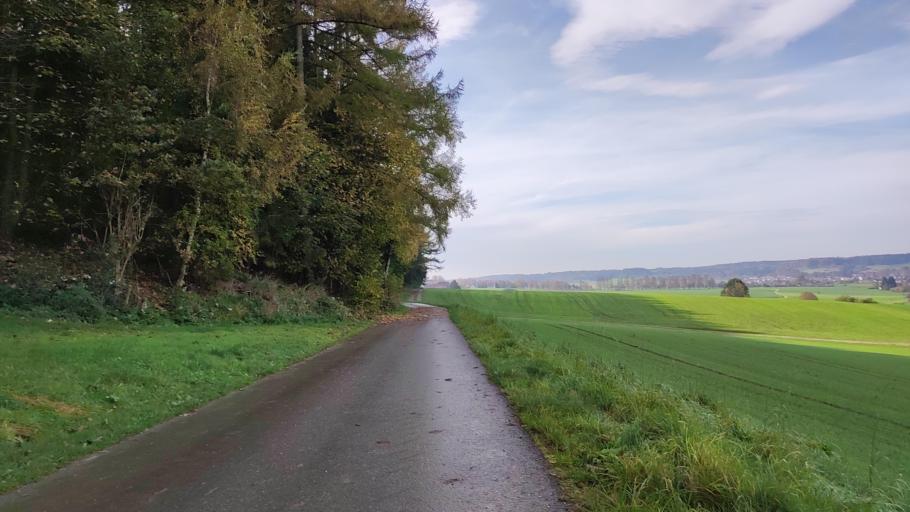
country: DE
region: Bavaria
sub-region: Swabia
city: Ziemetshausen
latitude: 48.2813
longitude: 10.5556
